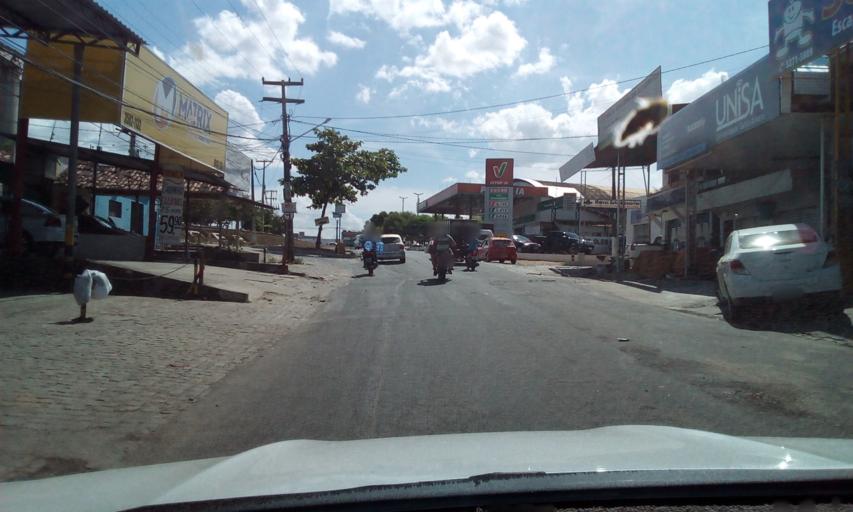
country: BR
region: Paraiba
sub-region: Guarabira
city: Guarabira
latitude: -6.8529
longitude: -35.4955
